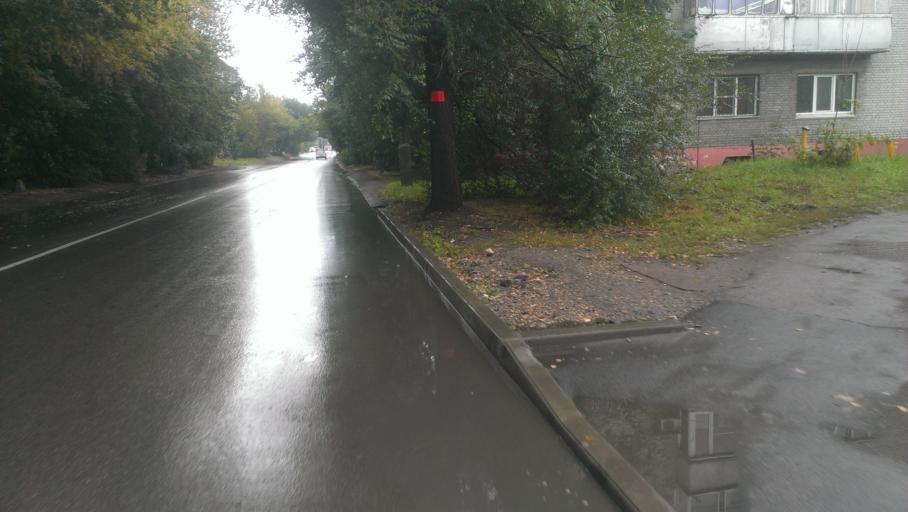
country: RU
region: Altai Krai
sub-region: Gorod Barnaulskiy
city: Barnaul
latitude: 53.3598
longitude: 83.7620
